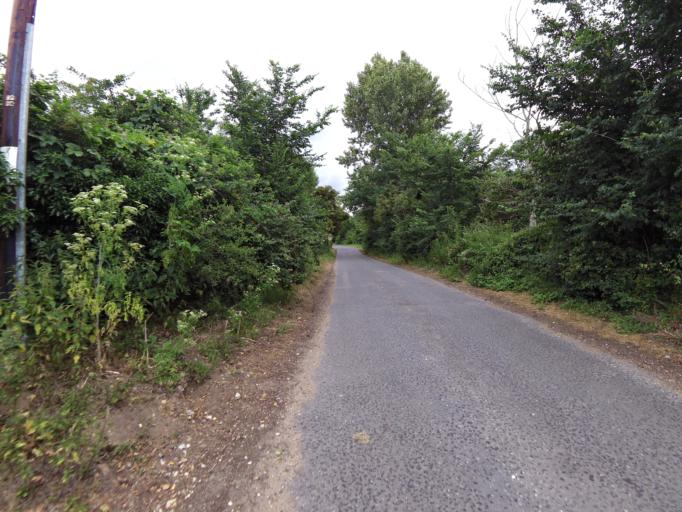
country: GB
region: England
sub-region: Suffolk
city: Bungay
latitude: 52.4374
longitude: 1.3894
